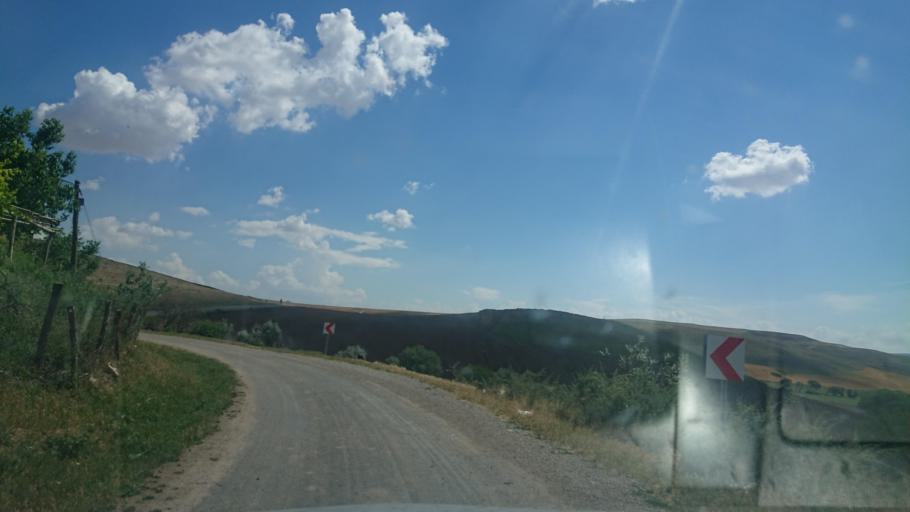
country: TR
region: Aksaray
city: Agacoren
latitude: 38.8267
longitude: 33.7915
